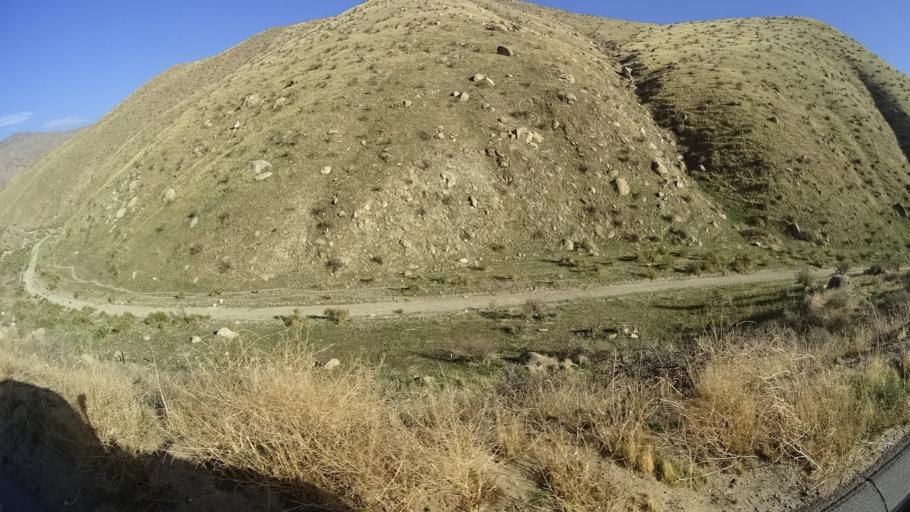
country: US
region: California
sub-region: Kern County
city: Bear Valley Springs
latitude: 35.3001
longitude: -118.6933
